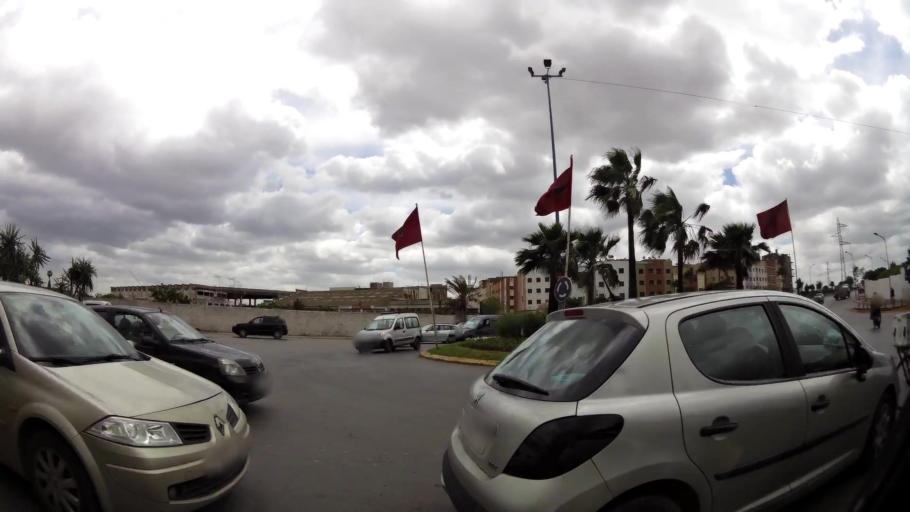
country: MA
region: Grand Casablanca
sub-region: Casablanca
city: Casablanca
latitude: 33.5871
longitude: -7.5463
